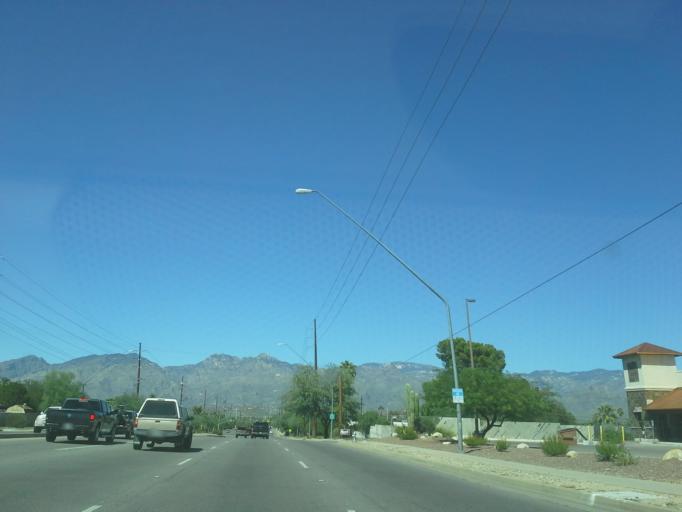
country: US
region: Arizona
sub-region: Pima County
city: Tucson
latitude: 32.2226
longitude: -110.8409
